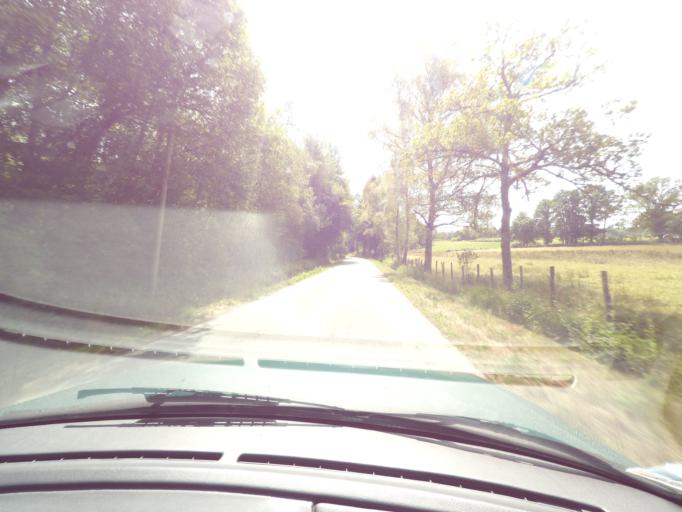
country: FR
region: Limousin
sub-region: Departement de la Correze
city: Bugeat
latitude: 45.7453
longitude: 1.9618
